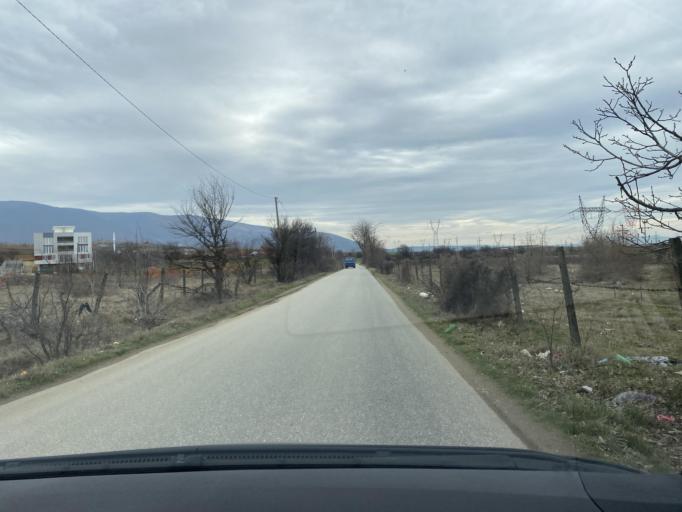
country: MK
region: Butel
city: Butel
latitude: 42.0414
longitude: 21.4584
